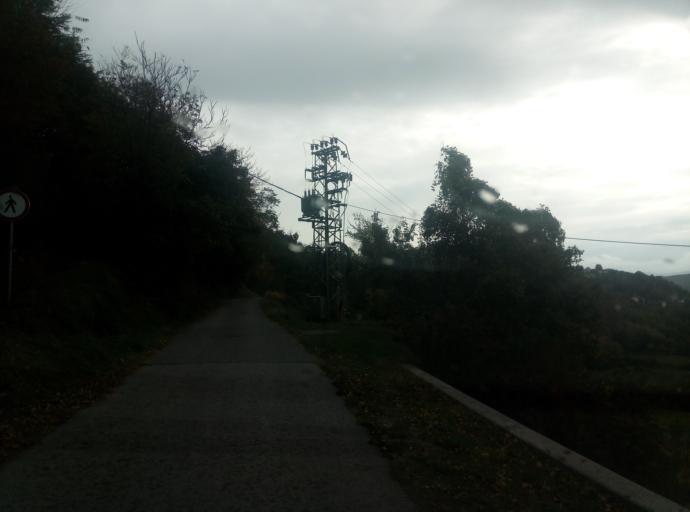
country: SI
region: Ajdovscina
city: Lokavec
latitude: 45.8227
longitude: 13.8456
